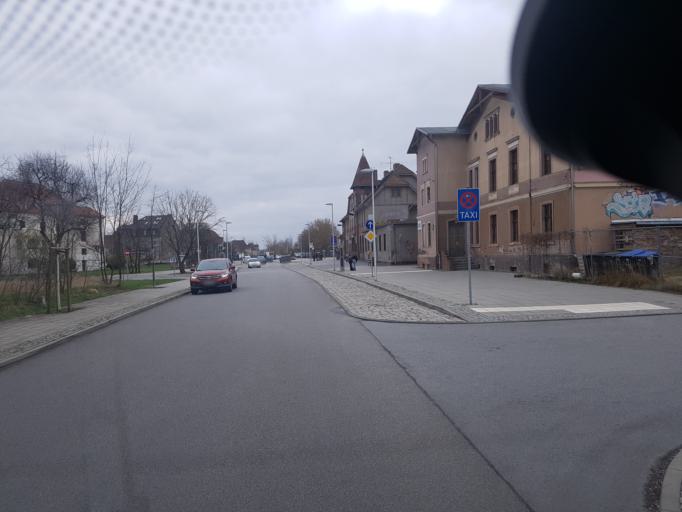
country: DE
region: Brandenburg
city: Eisenhuettenstadt
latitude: 52.1487
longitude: 14.6590
